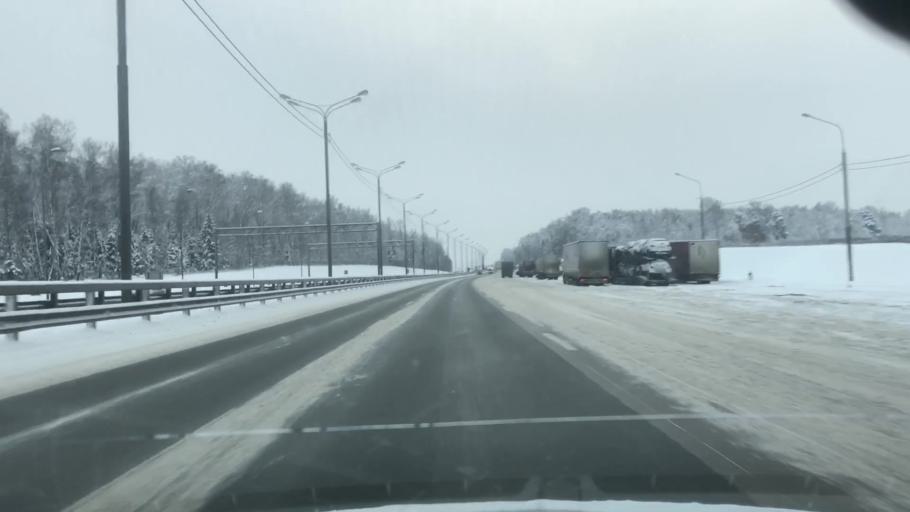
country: RU
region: Moskovskaya
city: Mikhnevo
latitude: 55.1817
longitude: 37.9049
